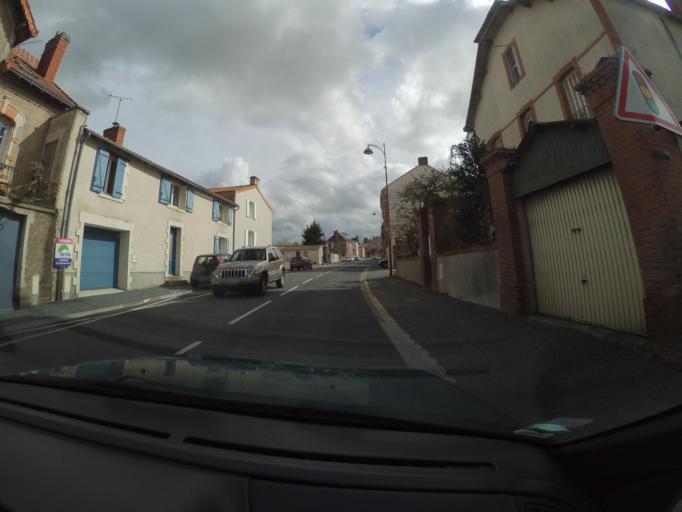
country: FR
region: Pays de la Loire
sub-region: Departement de Maine-et-Loire
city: Lire
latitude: 47.3459
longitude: -1.1629
